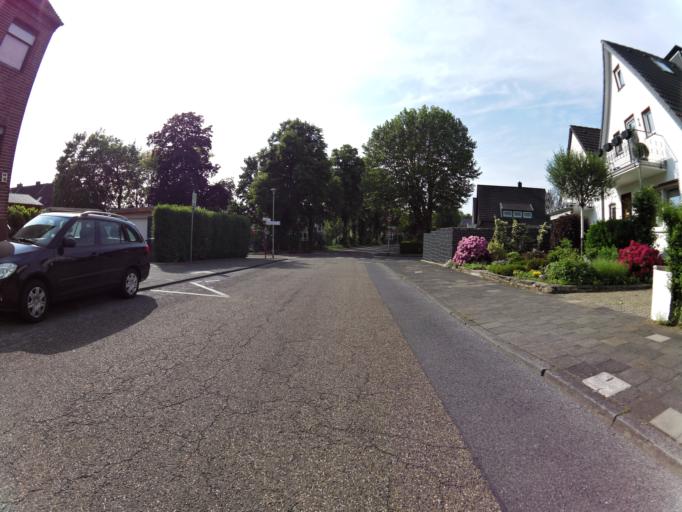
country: DE
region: North Rhine-Westphalia
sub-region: Regierungsbezirk Koln
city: Herzogenrath
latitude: 50.8721
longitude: 6.0994
